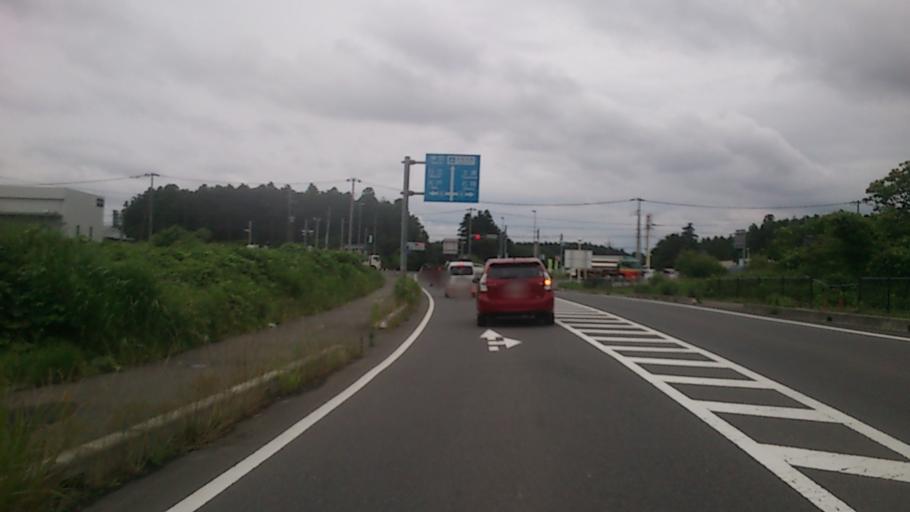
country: JP
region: Ibaraki
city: Ishioka
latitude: 36.2313
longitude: 140.3256
